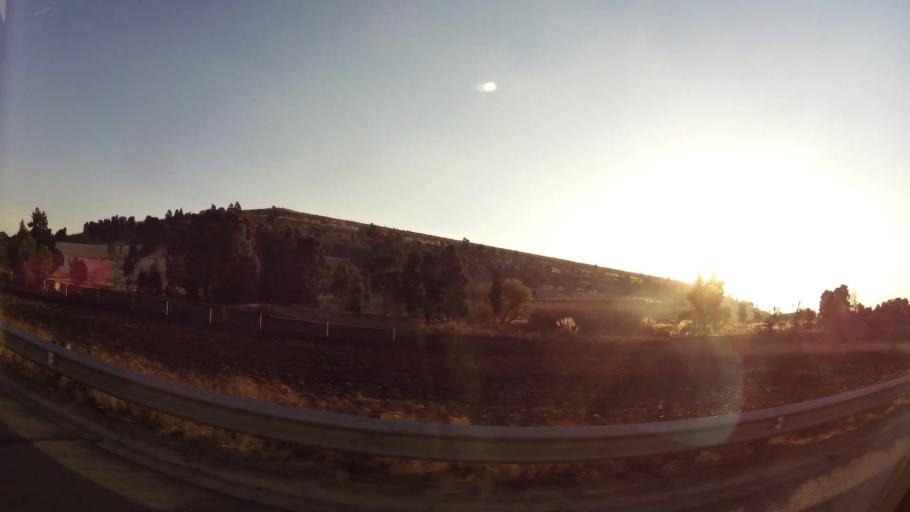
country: ZA
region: Gauteng
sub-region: City of Johannesburg Metropolitan Municipality
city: Johannesburg
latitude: -26.2250
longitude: 27.9613
